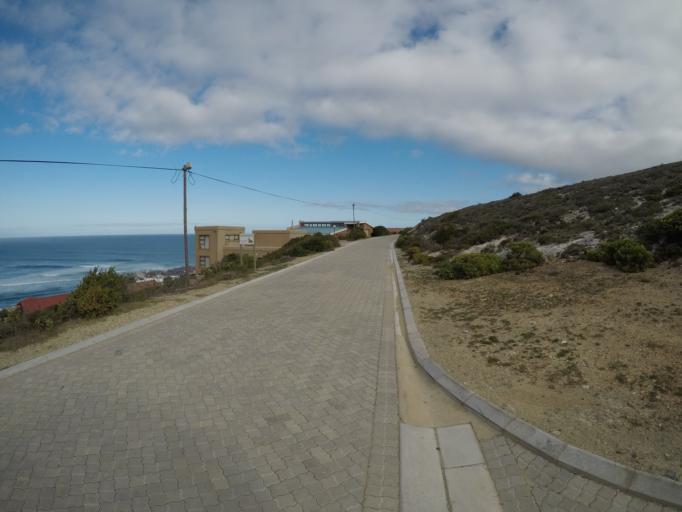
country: ZA
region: Western Cape
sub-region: Eden District Municipality
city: Riversdale
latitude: -34.4294
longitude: 21.3324
